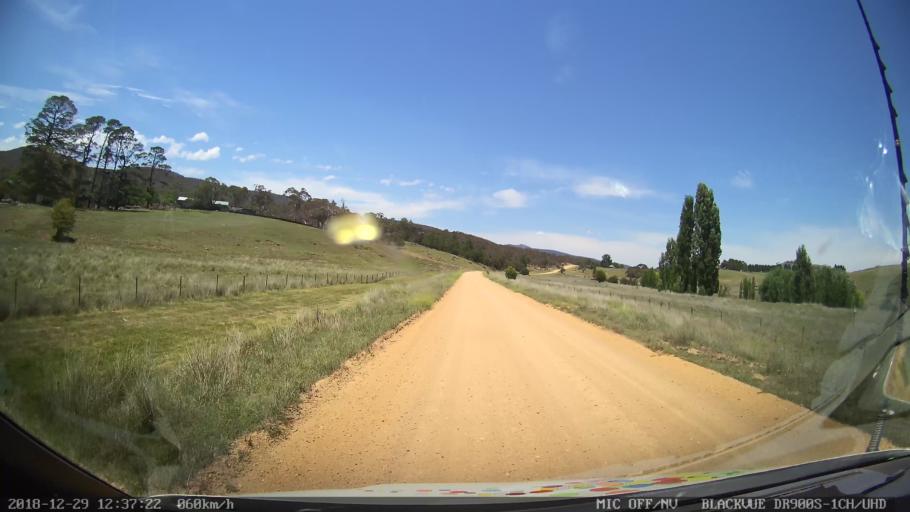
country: AU
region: Australian Capital Territory
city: Macarthur
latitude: -35.5794
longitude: 149.2279
